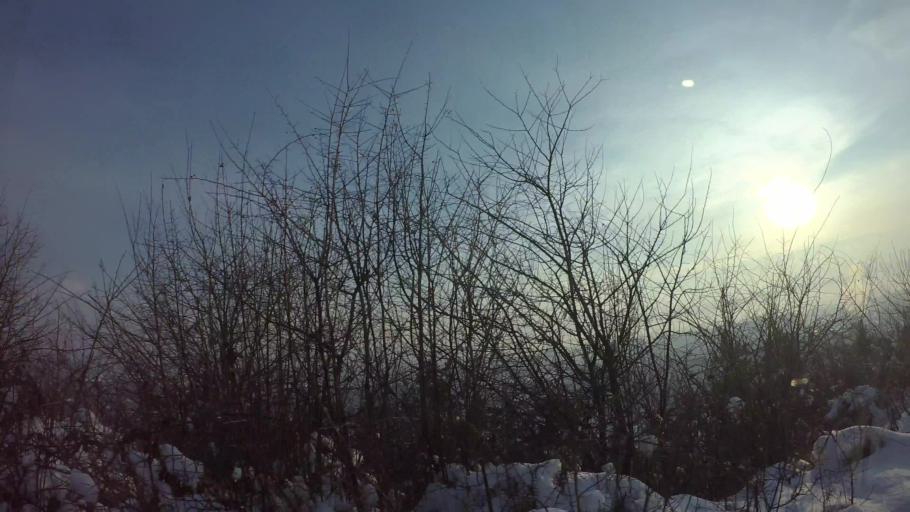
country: BA
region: Federation of Bosnia and Herzegovina
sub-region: Kanton Sarajevo
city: Sarajevo
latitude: 43.8340
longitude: 18.3486
